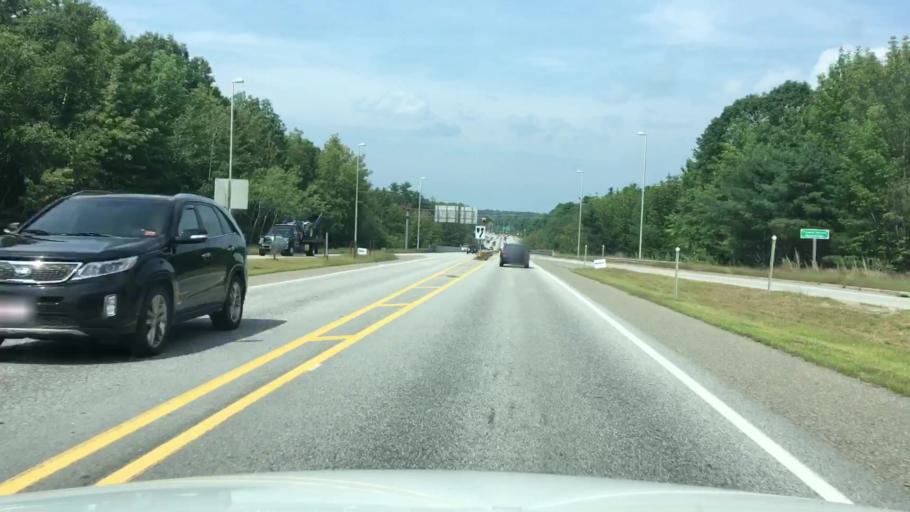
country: US
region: Maine
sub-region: Androscoggin County
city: Lewiston
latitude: 44.1136
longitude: -70.2112
